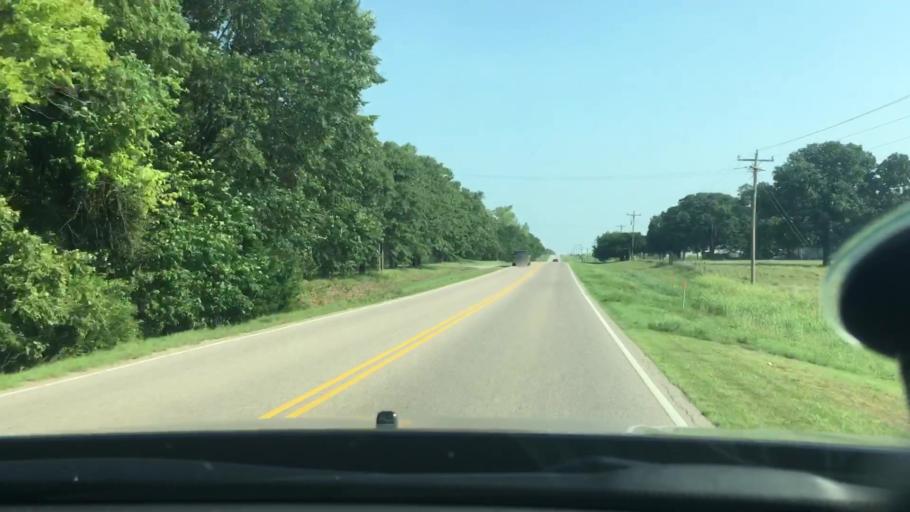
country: US
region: Oklahoma
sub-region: Johnston County
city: Tishomingo
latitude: 34.2720
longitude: -96.6711
